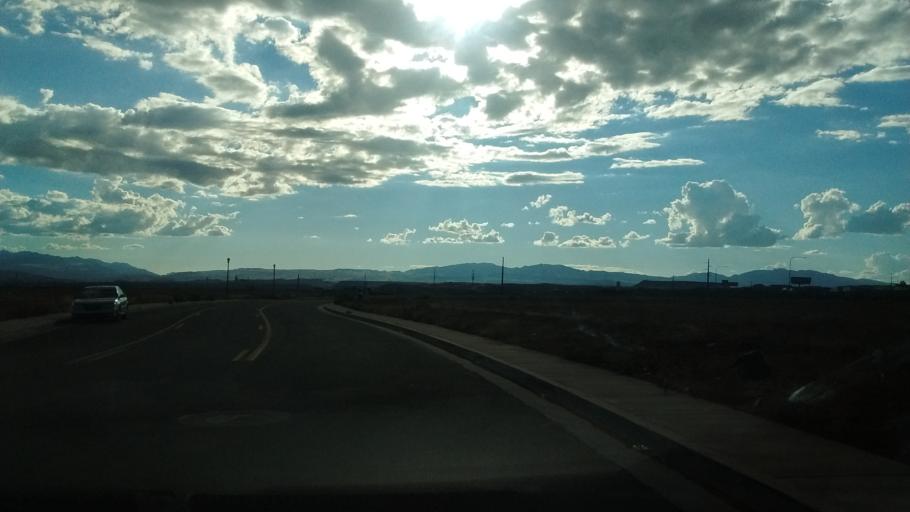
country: US
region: Utah
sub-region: Washington County
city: Washington
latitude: 37.1451
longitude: -113.4880
